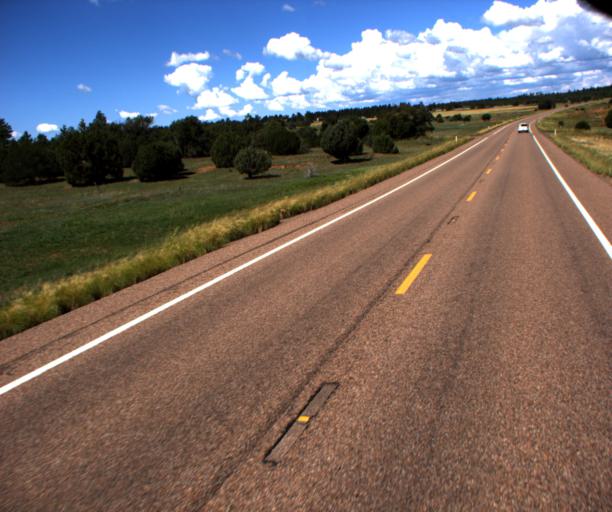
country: US
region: Arizona
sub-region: Navajo County
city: Linden
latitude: 34.3475
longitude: -110.3024
